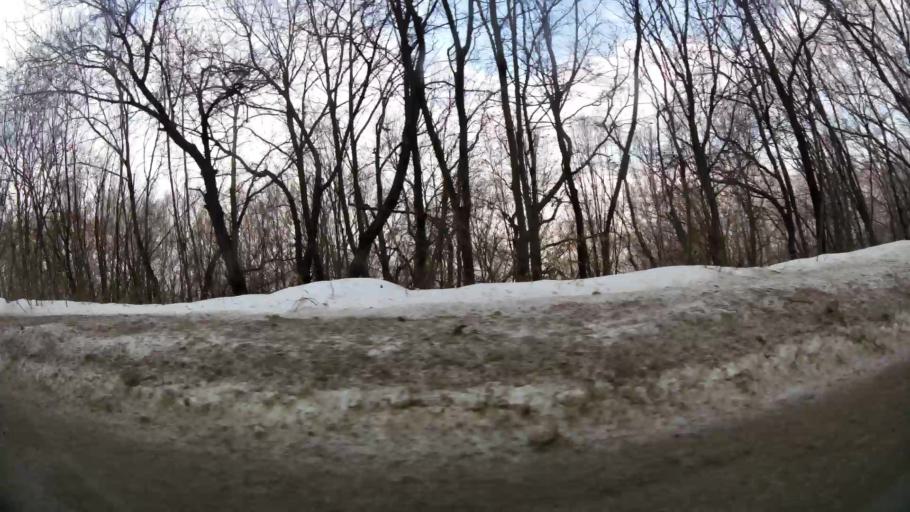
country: BG
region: Sofia-Capital
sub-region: Stolichna Obshtina
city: Sofia
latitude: 42.6439
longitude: 23.2347
